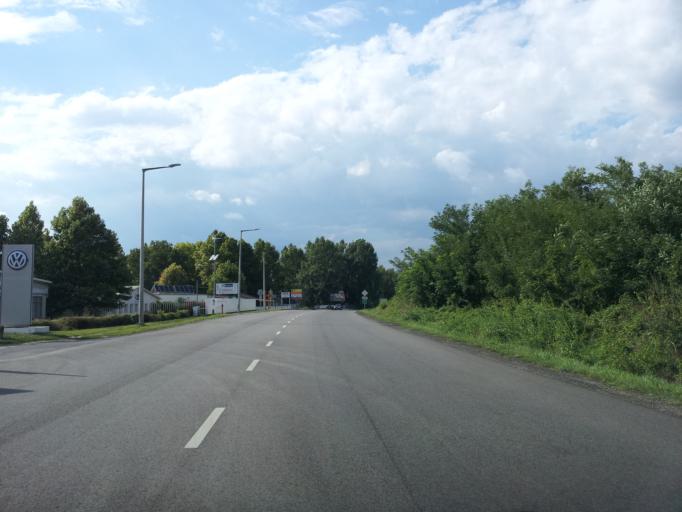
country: HU
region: Pest
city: Vac
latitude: 47.7971
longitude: 19.1096
